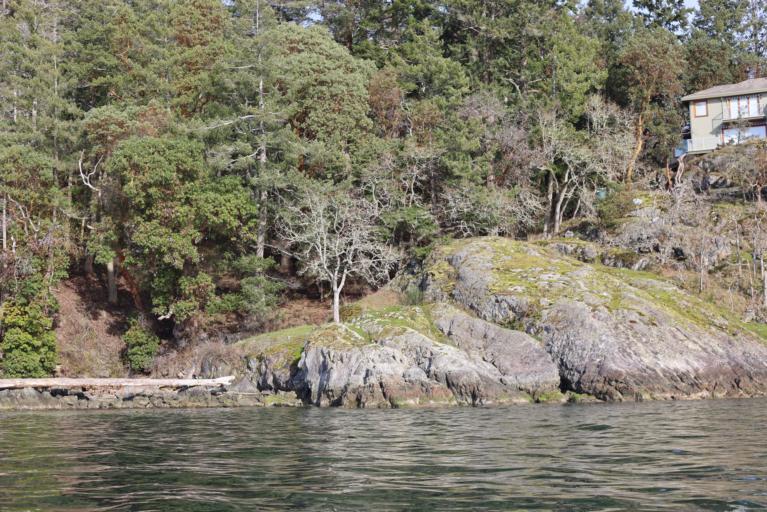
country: CA
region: British Columbia
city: Duncan
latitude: 48.7557
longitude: -123.6020
